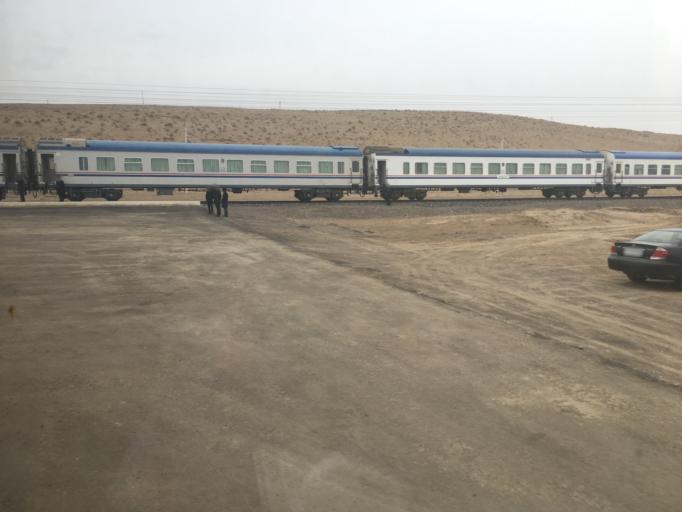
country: TM
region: Mary
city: Serhetabat
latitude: 35.4699
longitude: 62.4091
